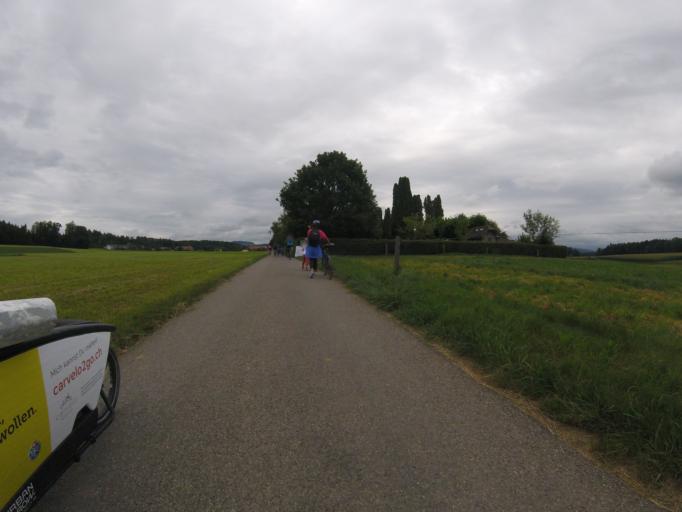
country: CH
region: Bern
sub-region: Bern-Mittelland District
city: Rubigen
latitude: 46.9100
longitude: 7.5493
